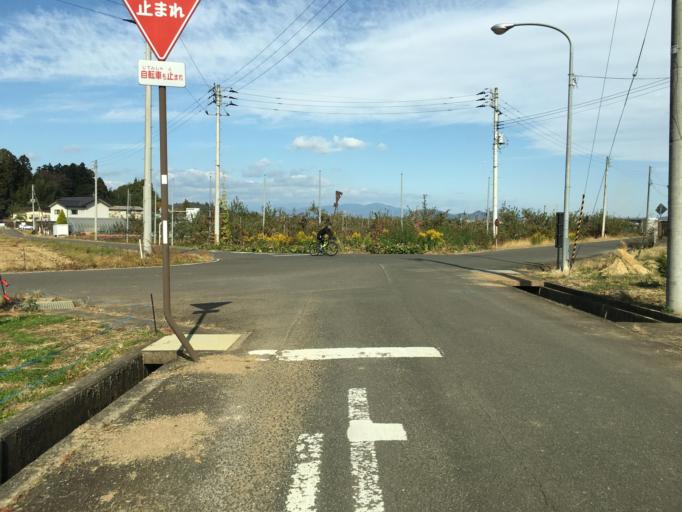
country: JP
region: Fukushima
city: Fukushima-shi
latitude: 37.7047
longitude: 140.4359
